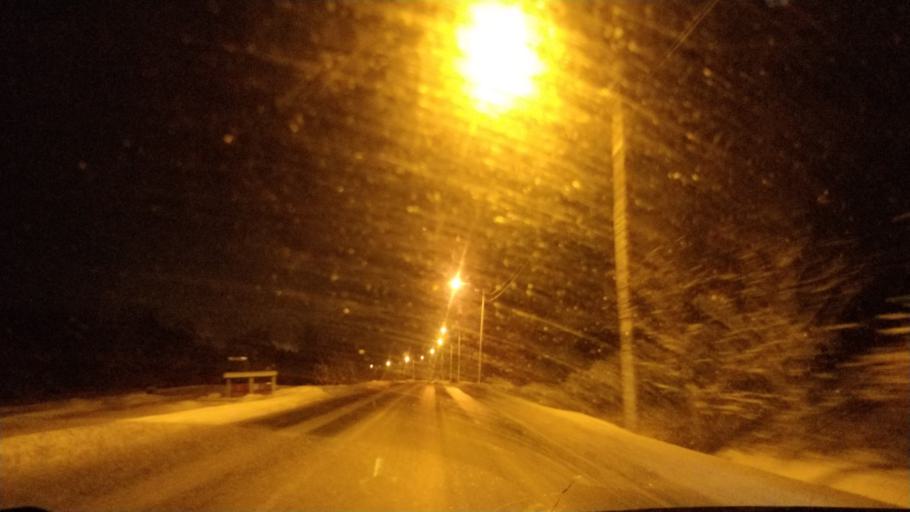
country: FI
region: Lapland
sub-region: Rovaniemi
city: Rovaniemi
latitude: 66.3895
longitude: 25.3782
